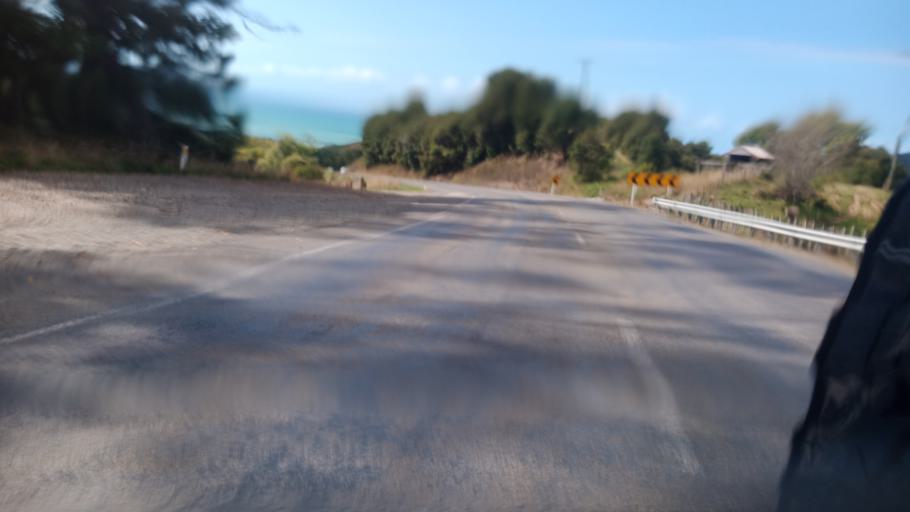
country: NZ
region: Gisborne
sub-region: Gisborne District
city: Gisborne
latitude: -38.1401
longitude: 178.2896
